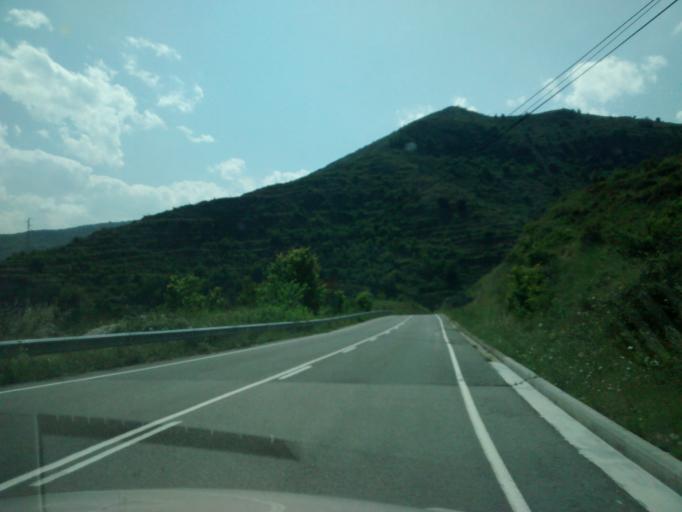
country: ES
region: La Rioja
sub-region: Provincia de La Rioja
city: Soto en Cameros
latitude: 42.2935
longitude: -2.4235
